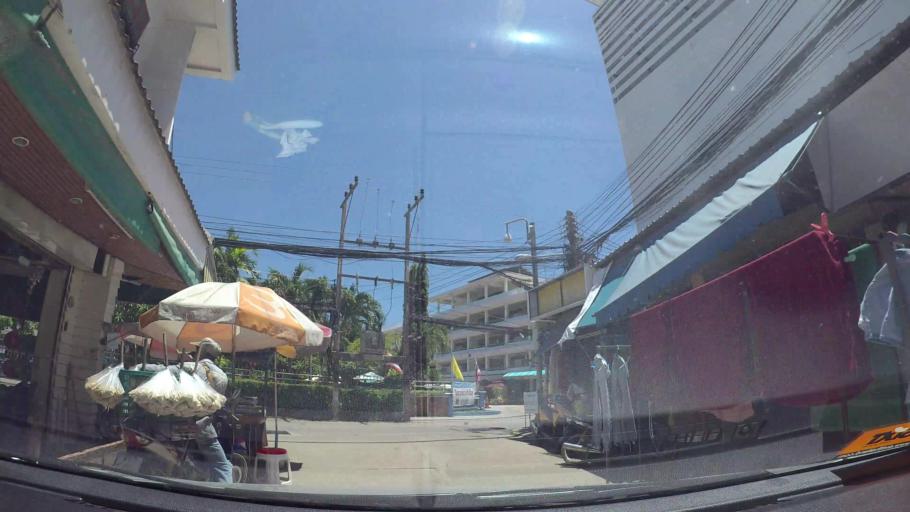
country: TH
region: Chon Buri
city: Phatthaya
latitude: 12.9317
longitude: 100.8944
